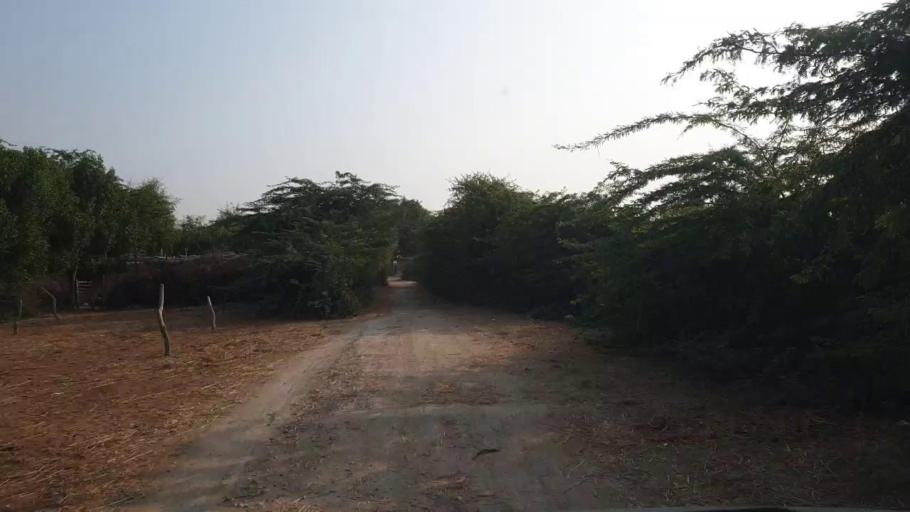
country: PK
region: Sindh
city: Rajo Khanani
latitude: 25.0326
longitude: 68.7772
